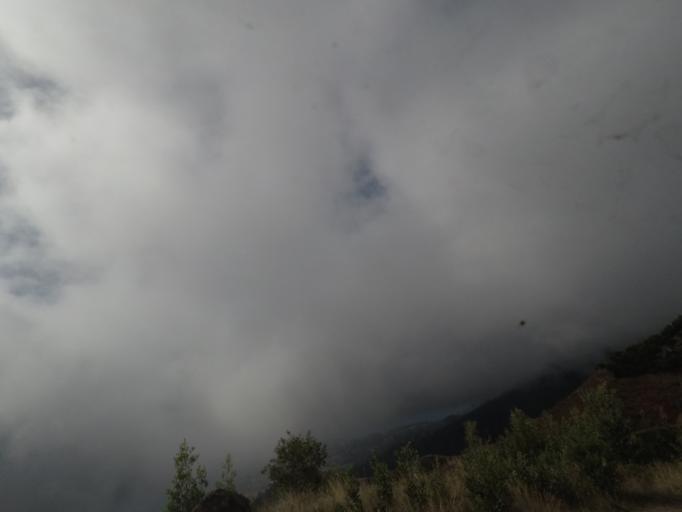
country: PT
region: Madeira
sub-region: Funchal
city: Nossa Senhora do Monte
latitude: 32.6980
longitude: -16.9104
